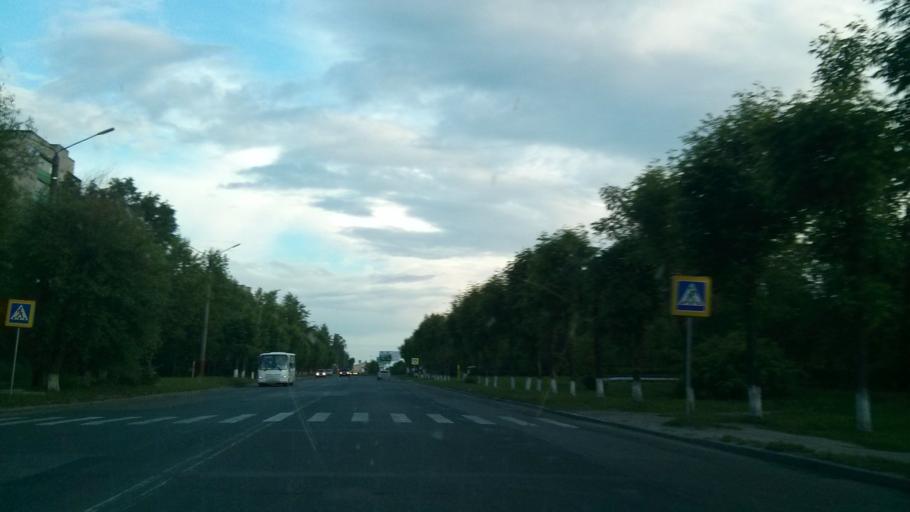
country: RU
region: Vladimir
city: Murom
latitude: 55.5519
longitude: 42.0628
